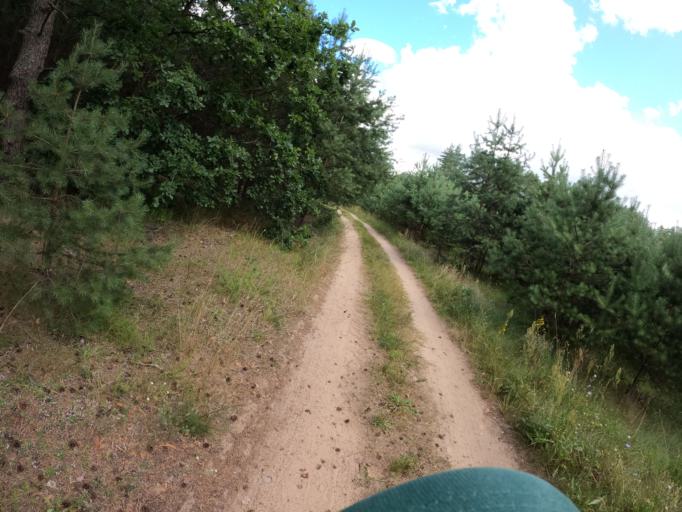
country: LT
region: Alytaus apskritis
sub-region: Alytus
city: Alytus
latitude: 54.5089
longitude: 24.0871
